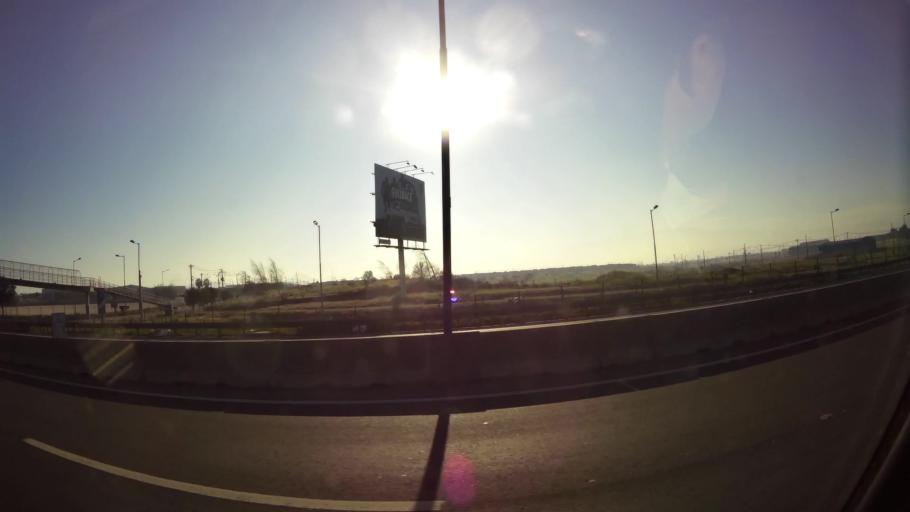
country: CL
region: Santiago Metropolitan
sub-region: Provincia de Santiago
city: Lo Prado
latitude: -33.4363
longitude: -70.7847
